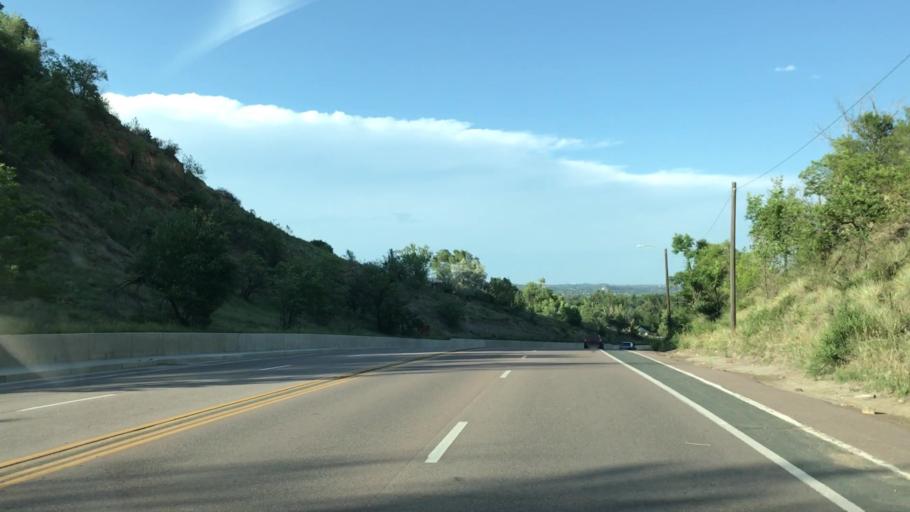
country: US
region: Colorado
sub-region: El Paso County
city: Colorado Springs
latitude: 38.8497
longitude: -104.8370
